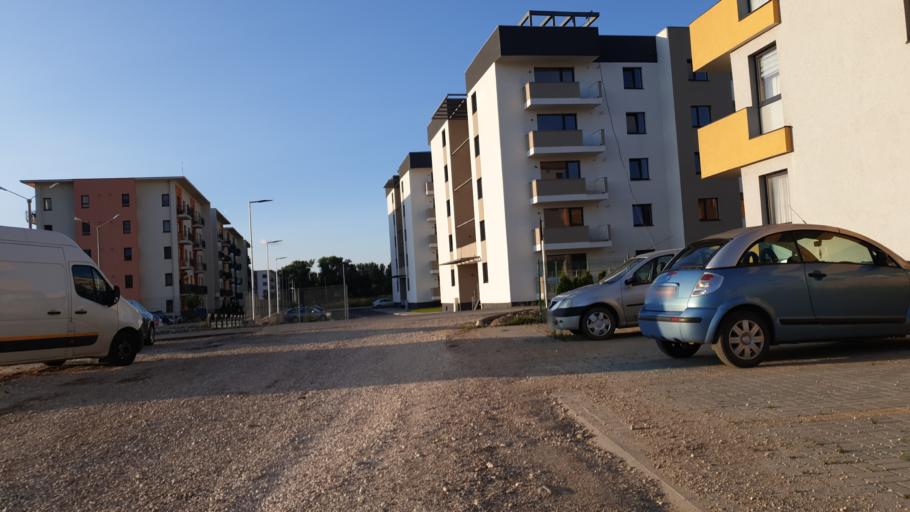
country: RO
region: Brasov
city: Brasov
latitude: 45.6791
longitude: 25.6071
